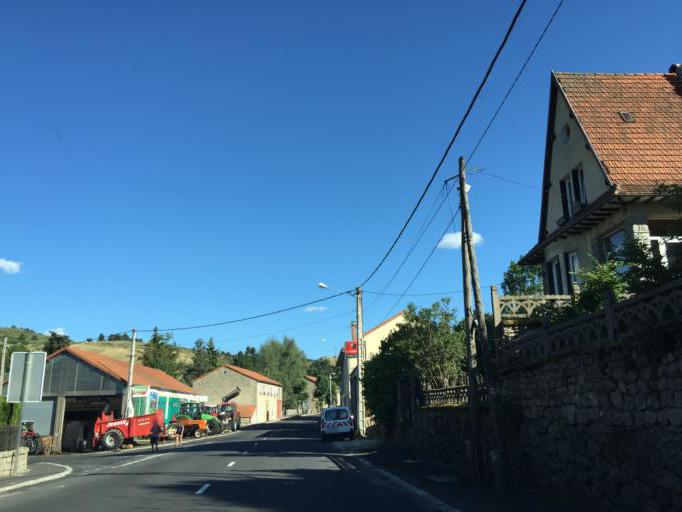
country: FR
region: Auvergne
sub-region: Departement de la Haute-Loire
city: Saugues
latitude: 44.9585
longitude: 3.5501
